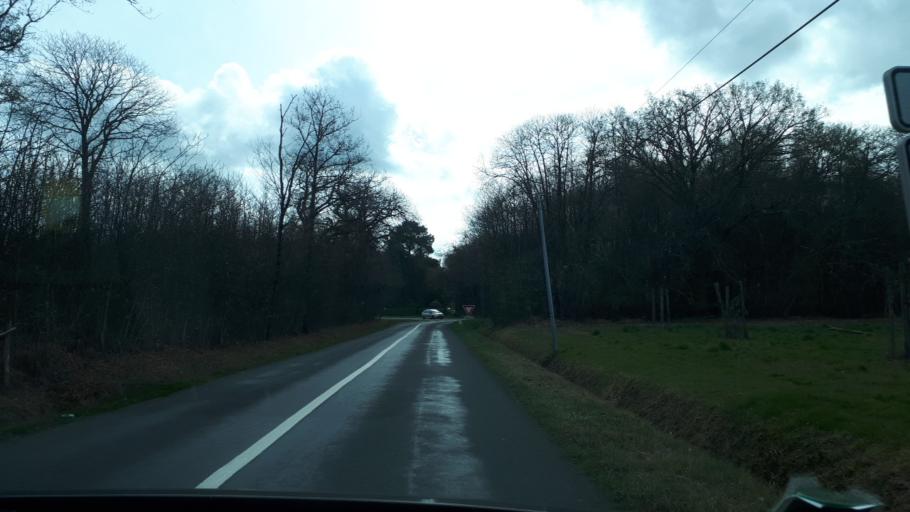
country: FR
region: Pays de la Loire
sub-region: Departement de la Sarthe
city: Le Grand-Luce
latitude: 47.8776
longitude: 0.4291
